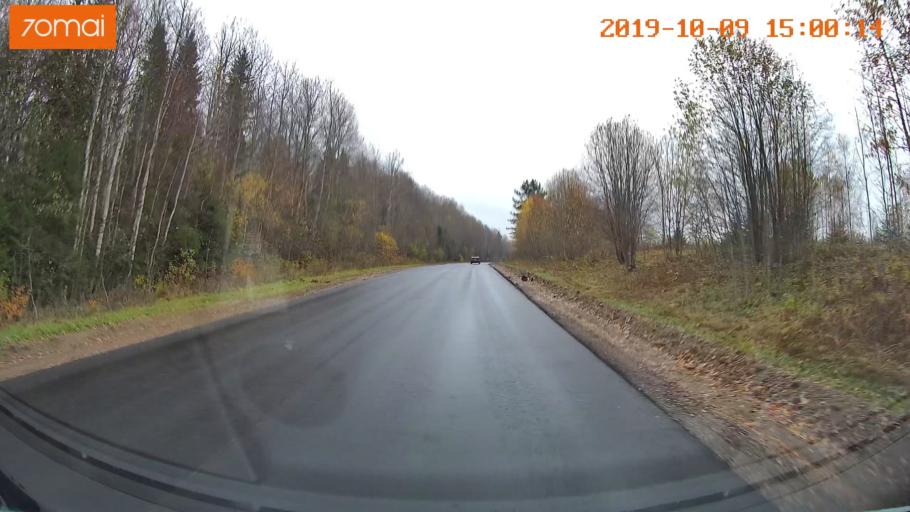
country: RU
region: Kostroma
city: Chistyye Bory
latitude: 58.3116
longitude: 41.6766
